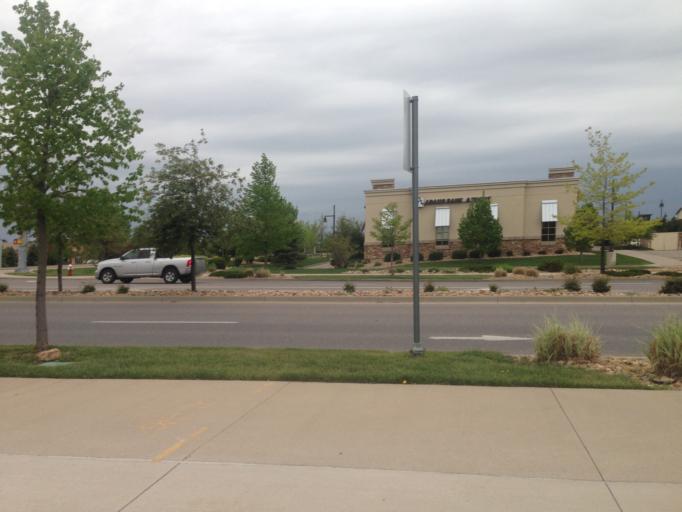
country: US
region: Colorado
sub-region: Boulder County
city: Longmont
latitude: 40.1530
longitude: -105.0927
